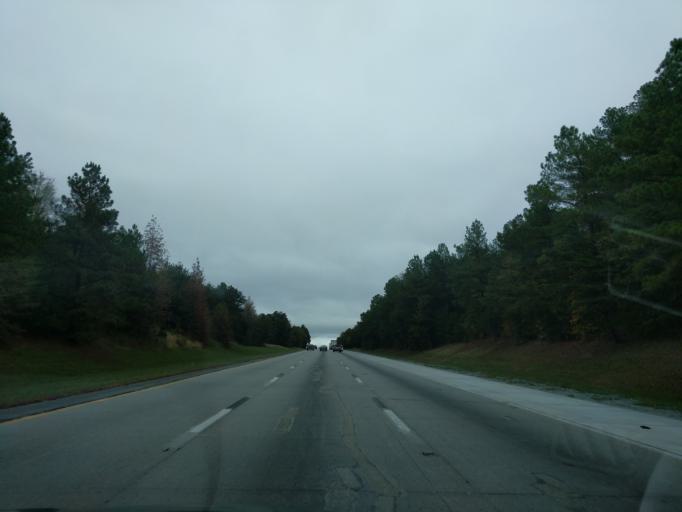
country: US
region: North Carolina
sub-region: Guilford County
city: Jamestown
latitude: 35.9495
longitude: -79.8995
